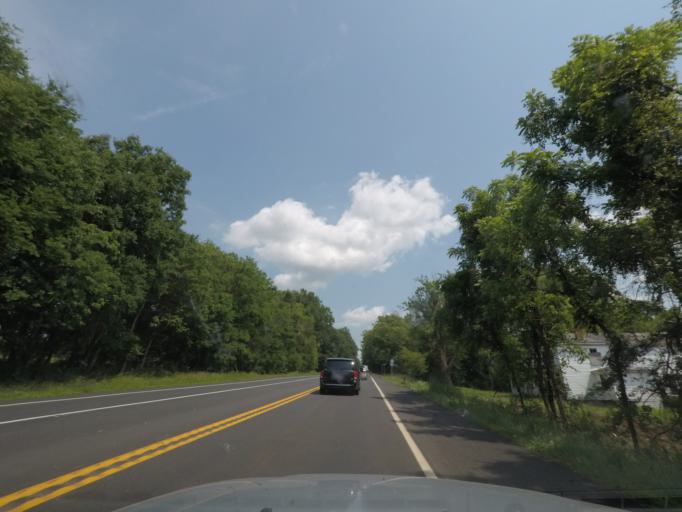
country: US
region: Virginia
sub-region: Orange County
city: Orange
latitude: 38.2789
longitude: -78.1376
